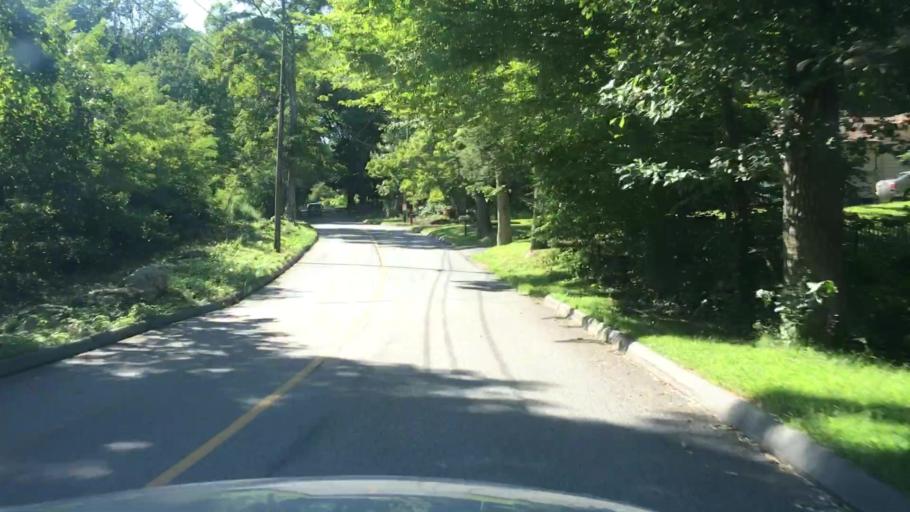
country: US
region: Connecticut
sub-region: Middlesex County
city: Deep River Center
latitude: 41.3681
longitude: -72.4444
